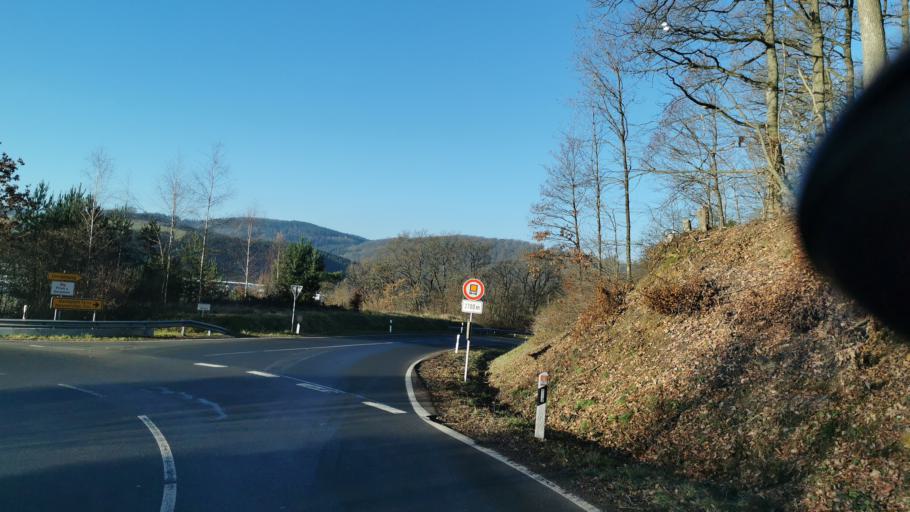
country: DE
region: Rheinland-Pfalz
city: Daun
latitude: 50.1961
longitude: 6.8092
